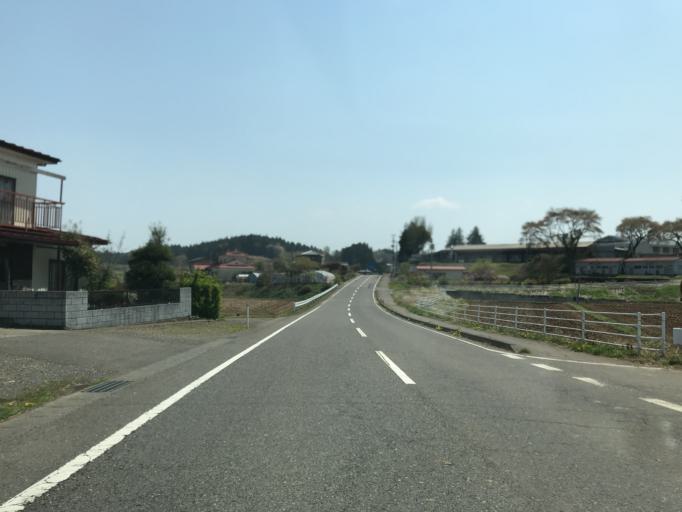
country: JP
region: Fukushima
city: Ishikawa
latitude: 37.1109
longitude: 140.3828
